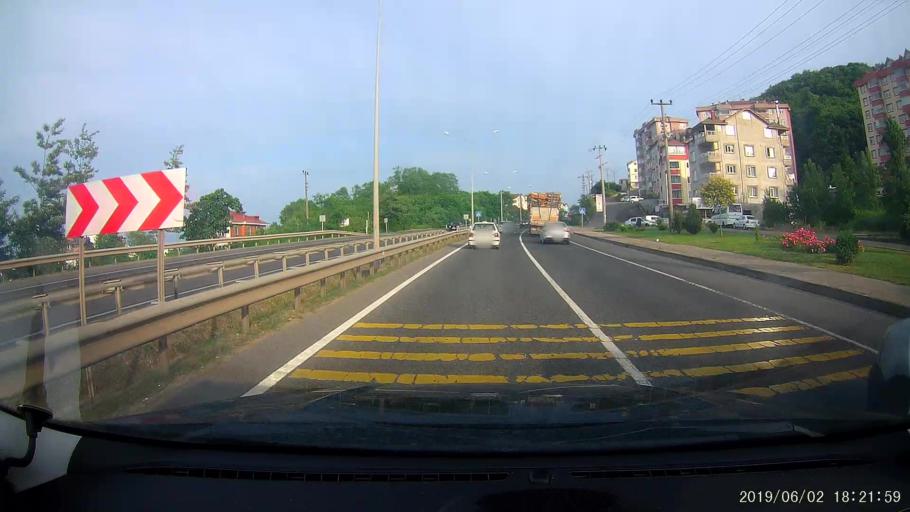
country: TR
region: Ordu
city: Fatsa
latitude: 41.0616
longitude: 37.4741
